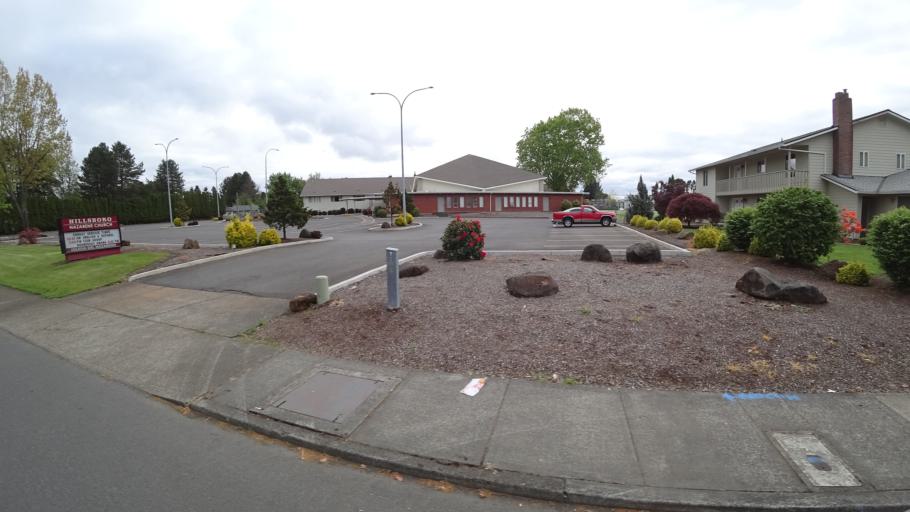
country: US
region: Oregon
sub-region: Washington County
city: Hillsboro
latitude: 45.5346
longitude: -122.9608
